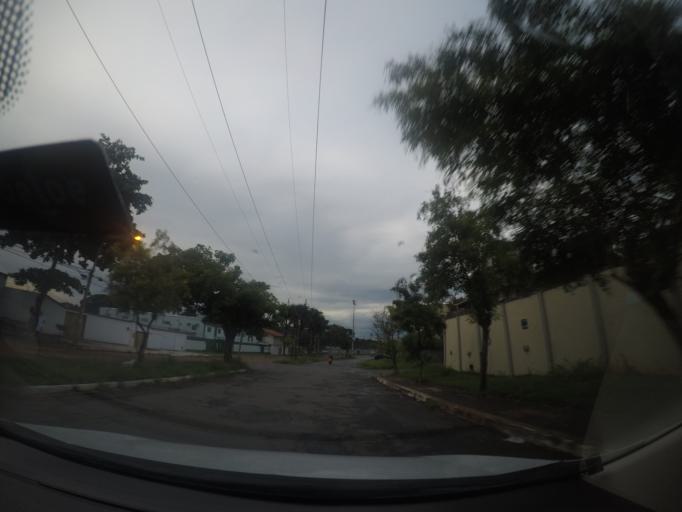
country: BR
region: Goias
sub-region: Goiania
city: Goiania
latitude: -16.6446
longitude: -49.2457
